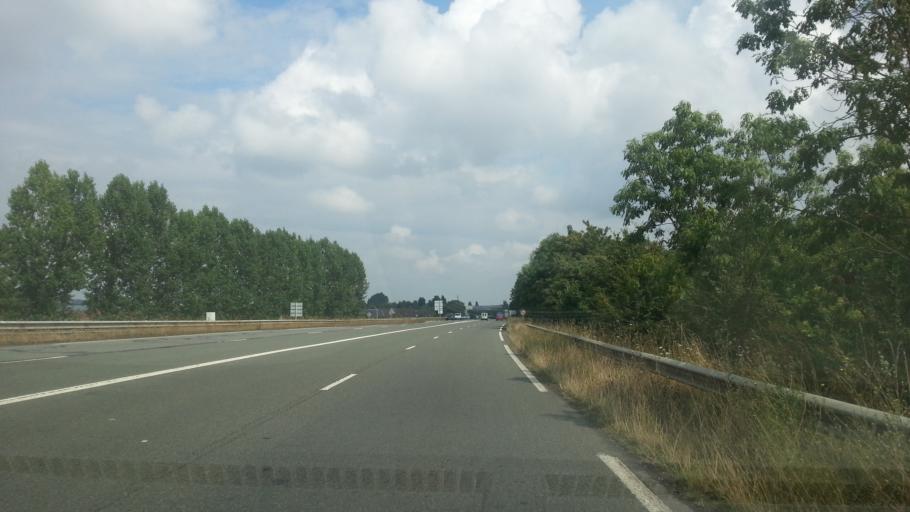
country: FR
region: Picardie
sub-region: Departement de l'Oise
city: Thiverny
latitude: 49.2530
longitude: 2.4432
